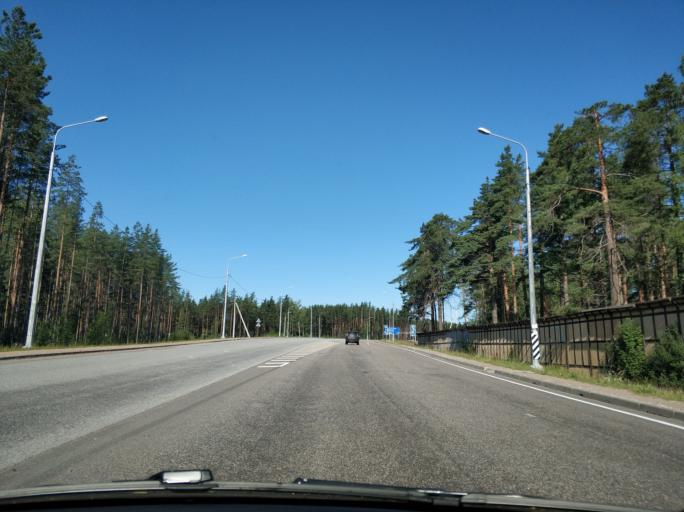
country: RU
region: Leningrad
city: Sapernoye
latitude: 60.6835
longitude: 29.9866
